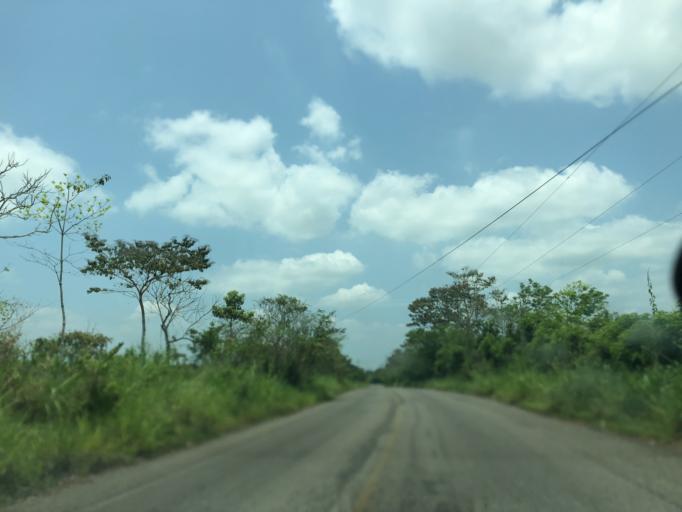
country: MX
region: Chiapas
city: Pueblo Juarez
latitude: 17.6272
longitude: -93.1656
